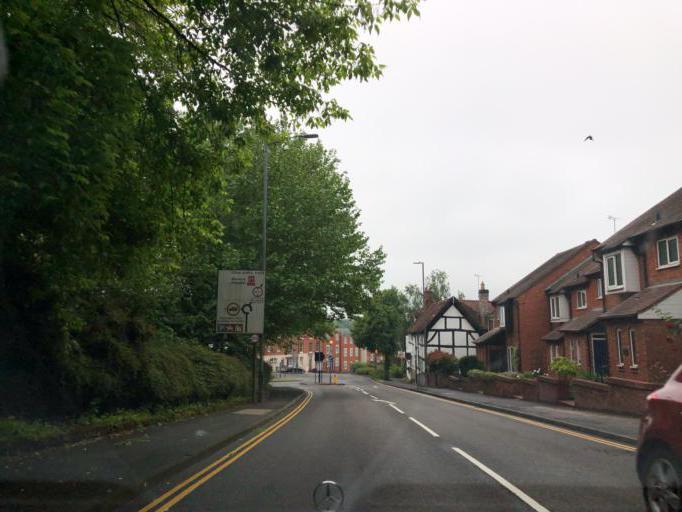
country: GB
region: England
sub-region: Warwickshire
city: Warwick
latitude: 52.2837
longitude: -1.5899
